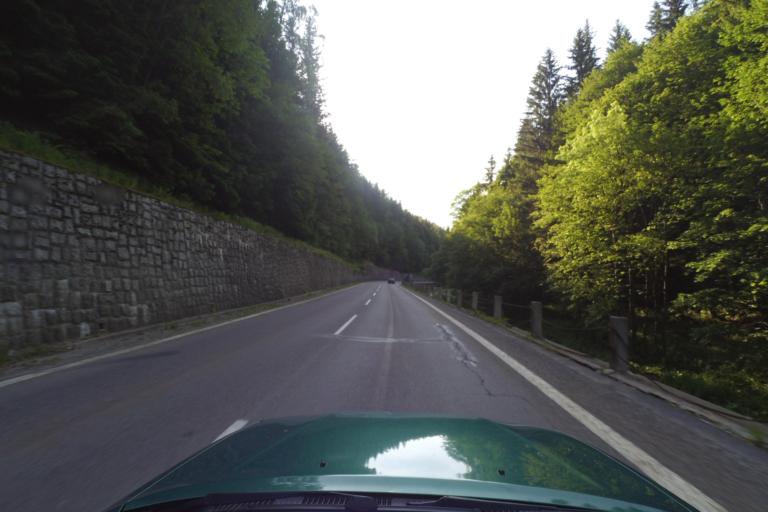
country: CZ
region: Kralovehradecky
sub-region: Okres Trutnov
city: Svoboda nad Upou
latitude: 50.6766
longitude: 15.7921
